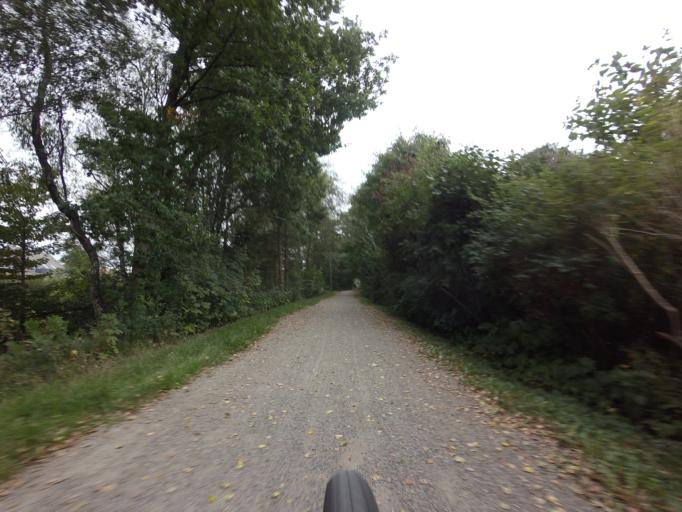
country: DK
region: Central Jutland
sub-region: Ikast-Brande Kommune
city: Brande
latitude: 55.9393
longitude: 9.1399
